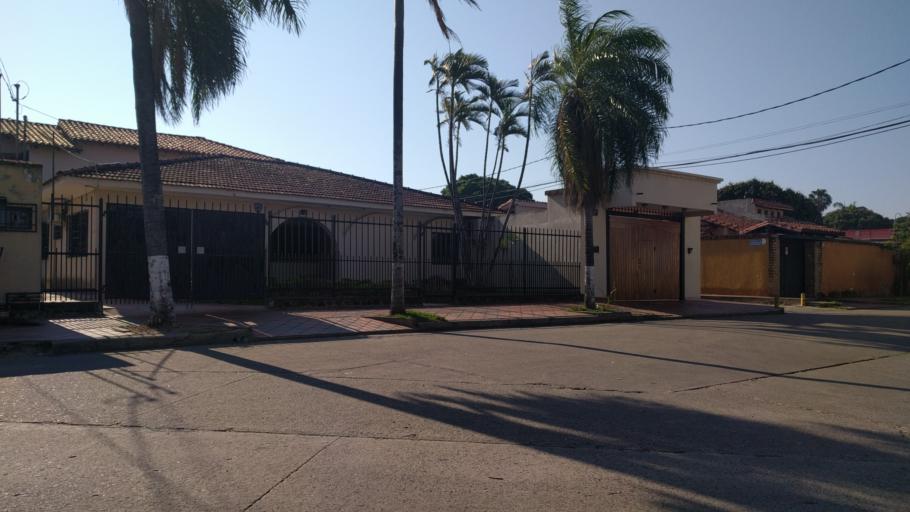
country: BO
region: Santa Cruz
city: Santa Cruz de la Sierra
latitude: -17.8095
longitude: -63.1809
